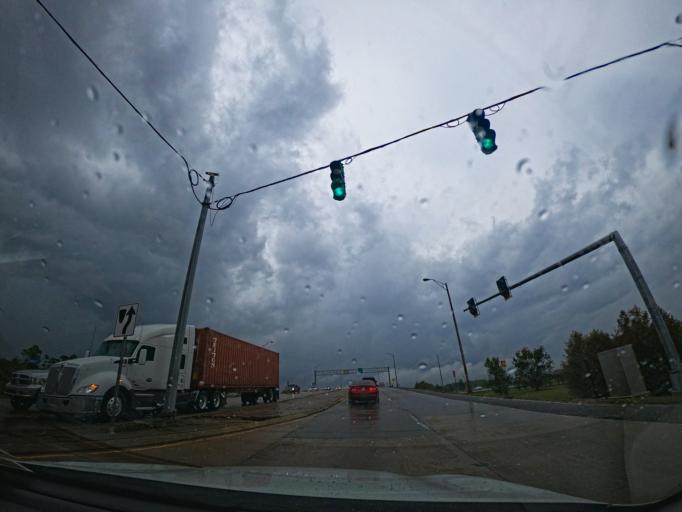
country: US
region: Louisiana
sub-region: Ouachita Parish
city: West Monroe
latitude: 32.5080
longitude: -92.1575
